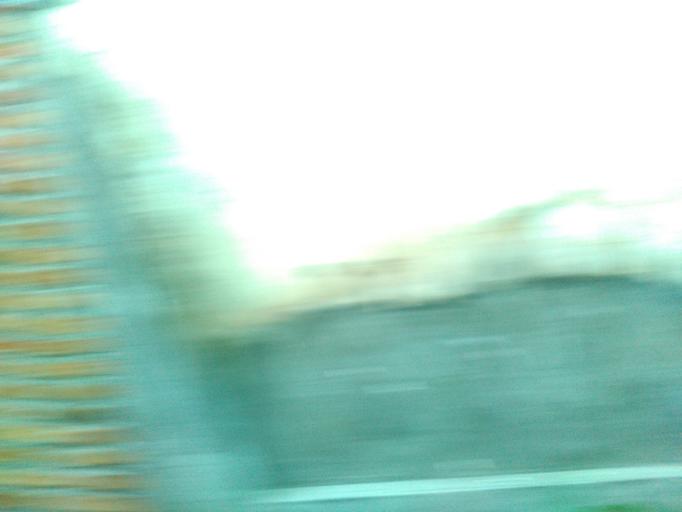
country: ID
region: Central Java
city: Ceper
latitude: -7.6560
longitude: 110.6952
